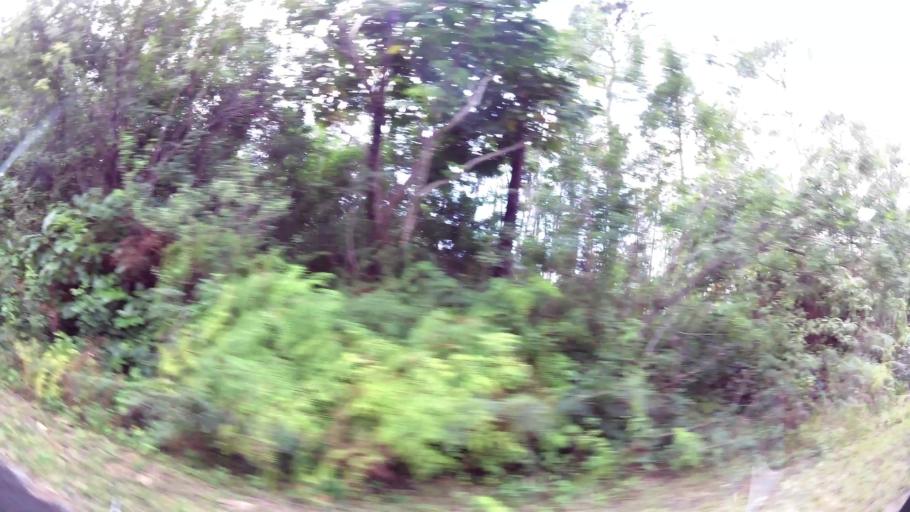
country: BS
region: Freeport
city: Lucaya
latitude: 26.5525
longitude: -78.5755
